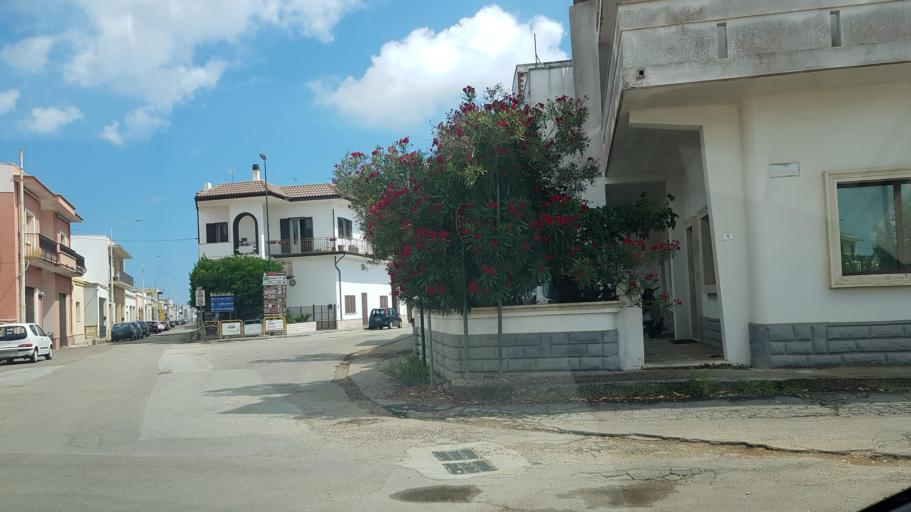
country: IT
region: Apulia
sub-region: Provincia di Lecce
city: Castrignano del Capo
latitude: 39.8379
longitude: 18.3455
